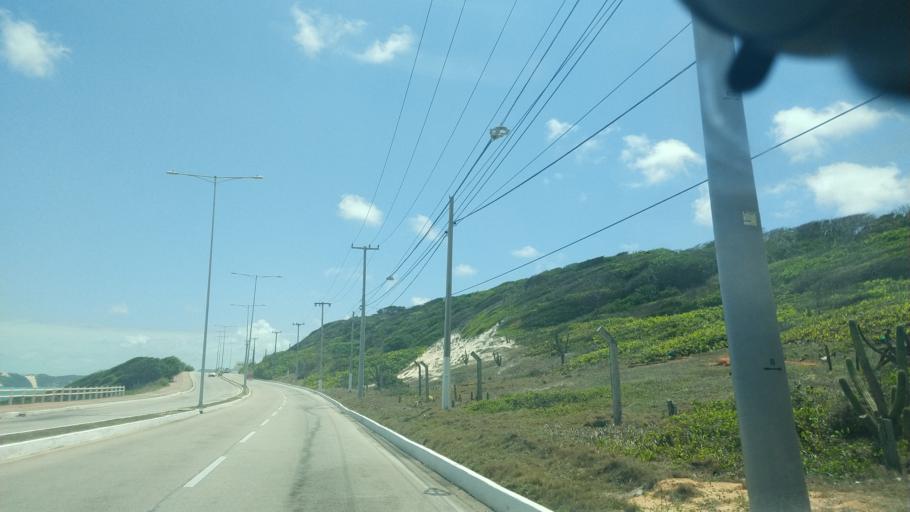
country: BR
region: Rio Grande do Norte
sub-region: Natal
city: Natal
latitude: -5.8370
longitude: -35.1825
